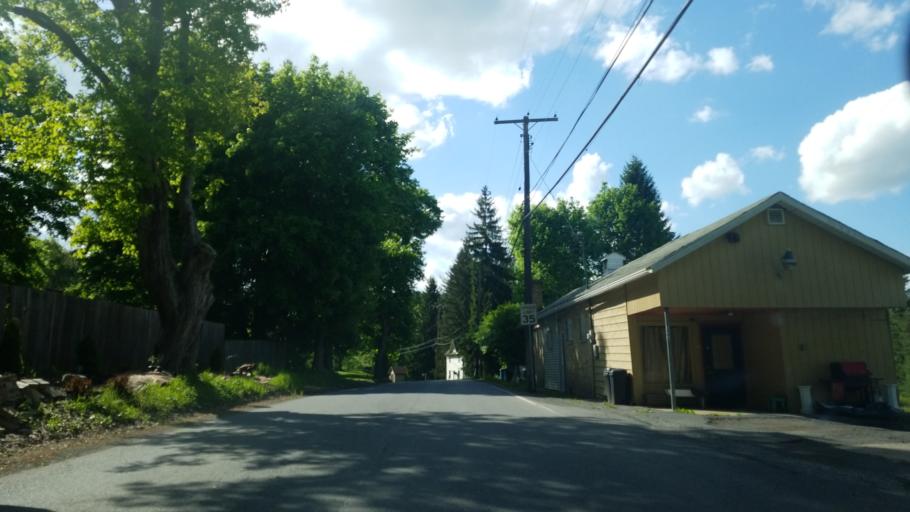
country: US
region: Pennsylvania
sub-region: Clearfield County
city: Troy
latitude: 40.9275
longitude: -78.2801
